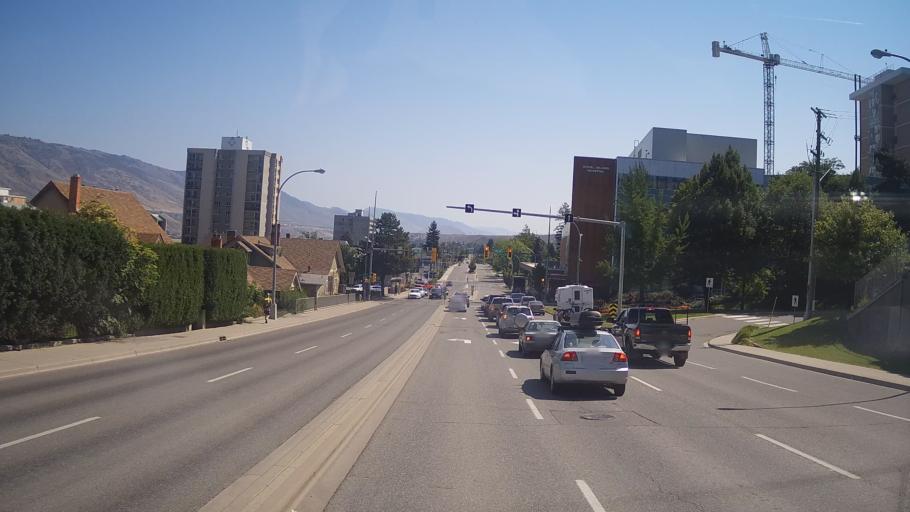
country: CA
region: British Columbia
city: Kamloops
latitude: 50.6714
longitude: -120.3361
